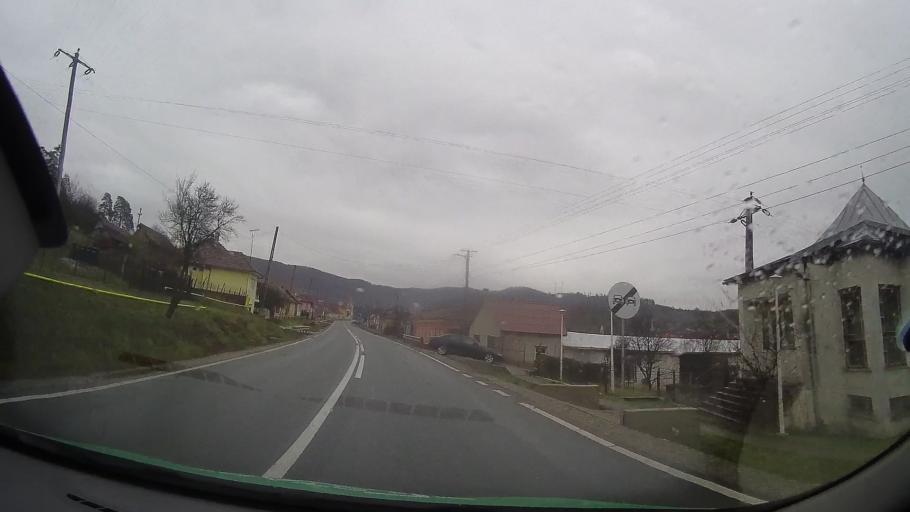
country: RO
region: Bistrita-Nasaud
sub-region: Comuna Teaca
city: Teaca
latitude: 46.9134
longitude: 24.4990
